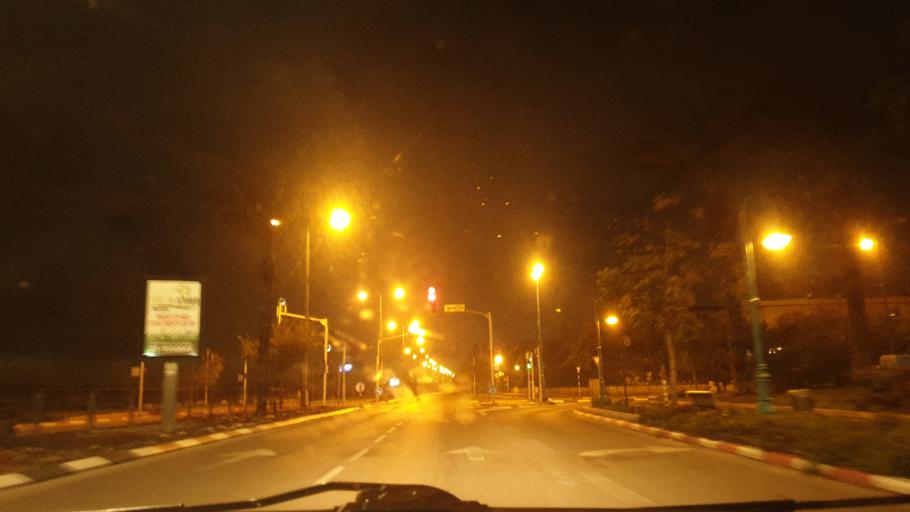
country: IL
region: Central District
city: Bet Dagan
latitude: 31.9740
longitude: 34.8169
